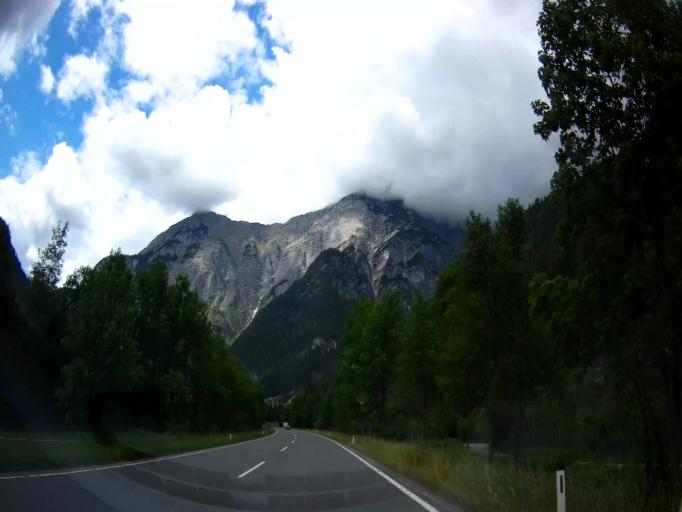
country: AT
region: Salzburg
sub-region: Politischer Bezirk Zell am See
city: Saalfelden am Steinernen Meer
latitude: 47.4742
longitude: 12.8327
